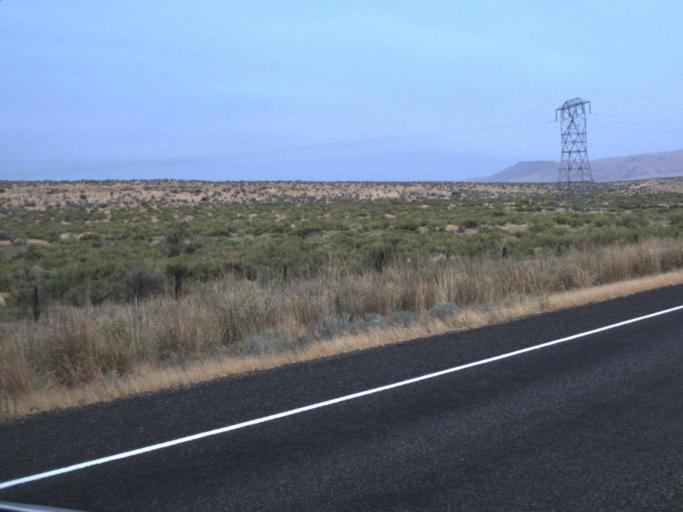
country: US
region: Washington
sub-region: Yakima County
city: Toppenish
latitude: 46.2386
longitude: -120.4189
